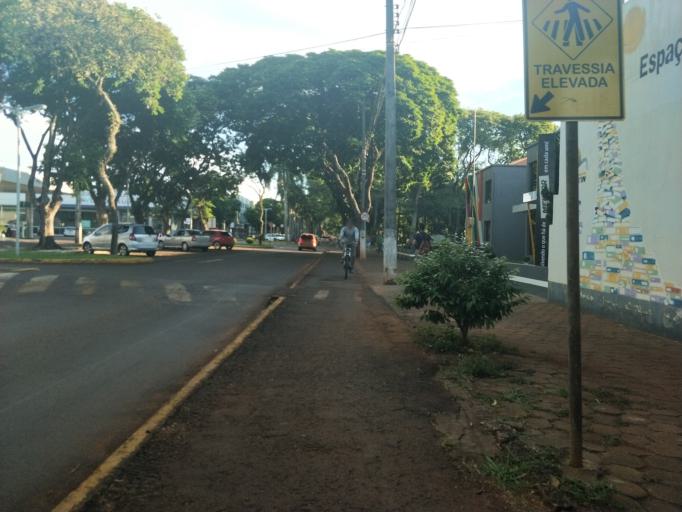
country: BR
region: Parana
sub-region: Marechal Candido Rondon
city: Marechal Candido Rondon
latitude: -24.5562
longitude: -54.0566
